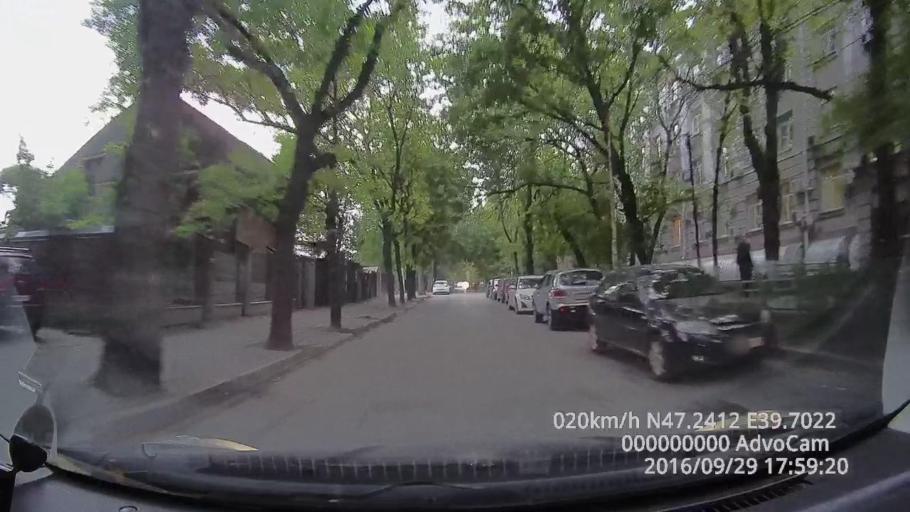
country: RU
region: Rostov
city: Rostov-na-Donu
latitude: 47.2412
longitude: 39.7025
